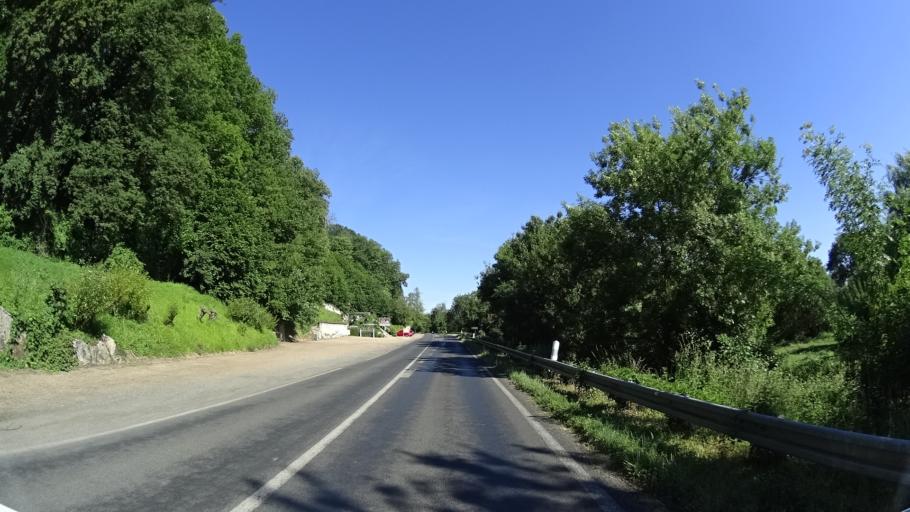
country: FR
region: Pays de la Loire
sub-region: Departement de Maine-et-Loire
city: Saumur
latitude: 47.2817
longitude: -0.1217
